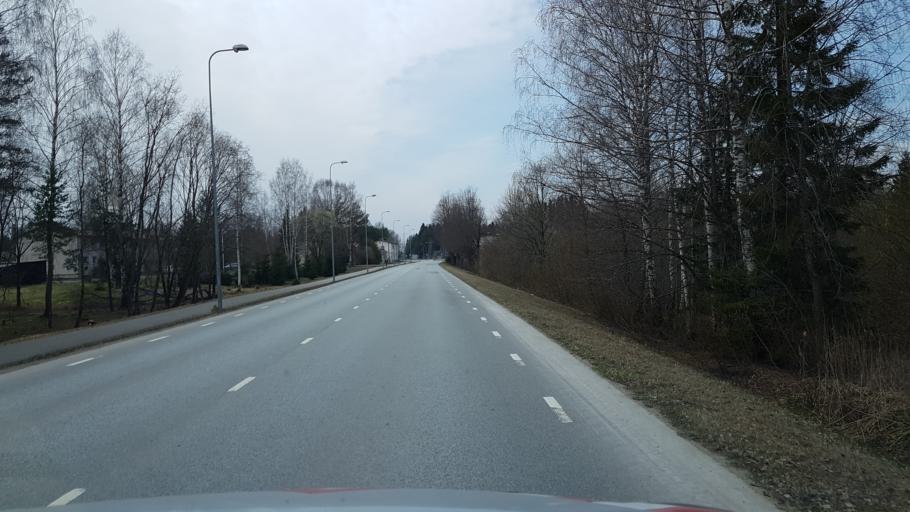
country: EE
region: Ida-Virumaa
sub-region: Aseri vald
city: Aseri
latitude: 59.3516
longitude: 26.8273
